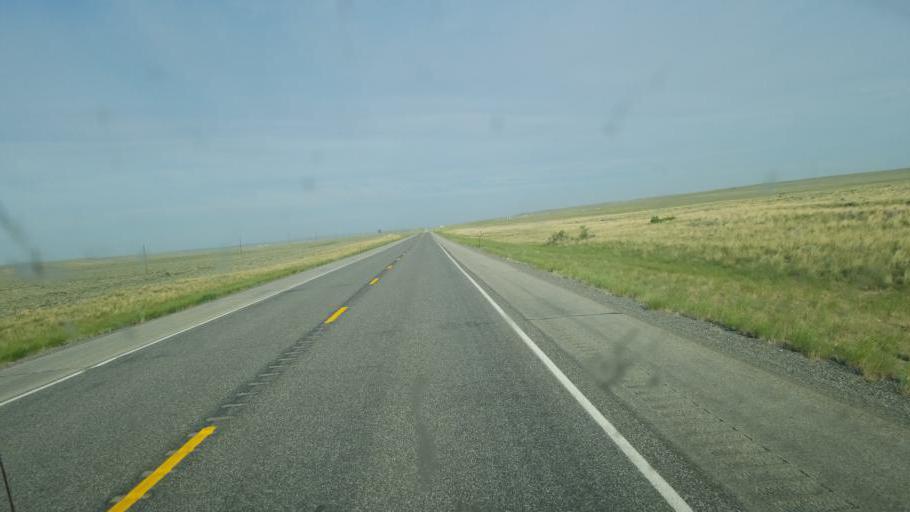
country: US
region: Wyoming
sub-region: Hot Springs County
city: Thermopolis
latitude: 43.1424
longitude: -107.5048
